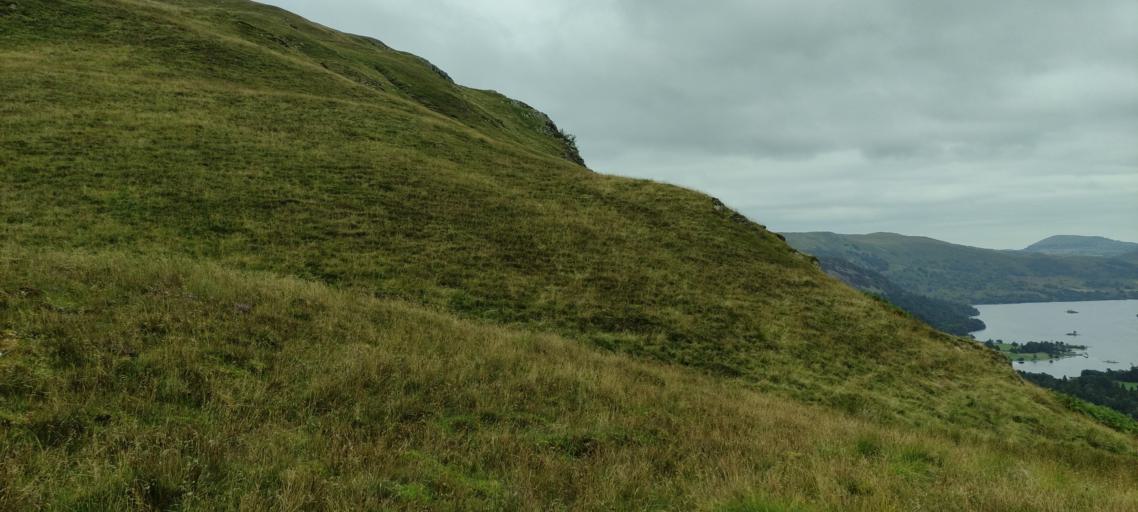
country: GB
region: England
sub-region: Cumbria
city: Ambleside
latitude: 54.5206
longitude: -2.9477
